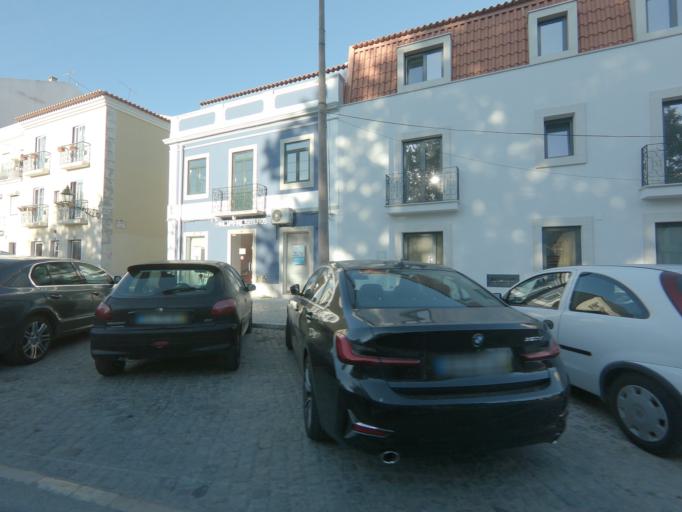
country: PT
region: Setubal
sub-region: Setubal
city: Setubal
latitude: 38.5235
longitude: -8.8983
